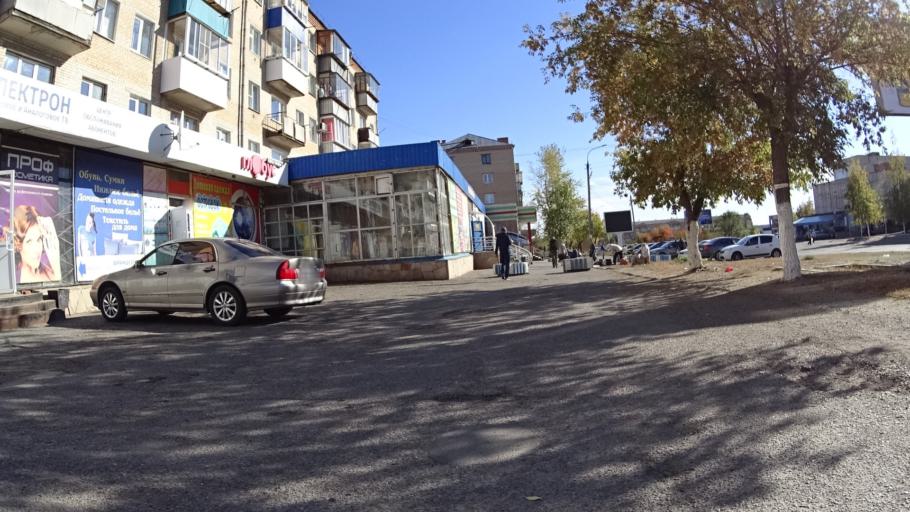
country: RU
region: Chelyabinsk
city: Troitsk
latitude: 54.0788
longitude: 61.5302
